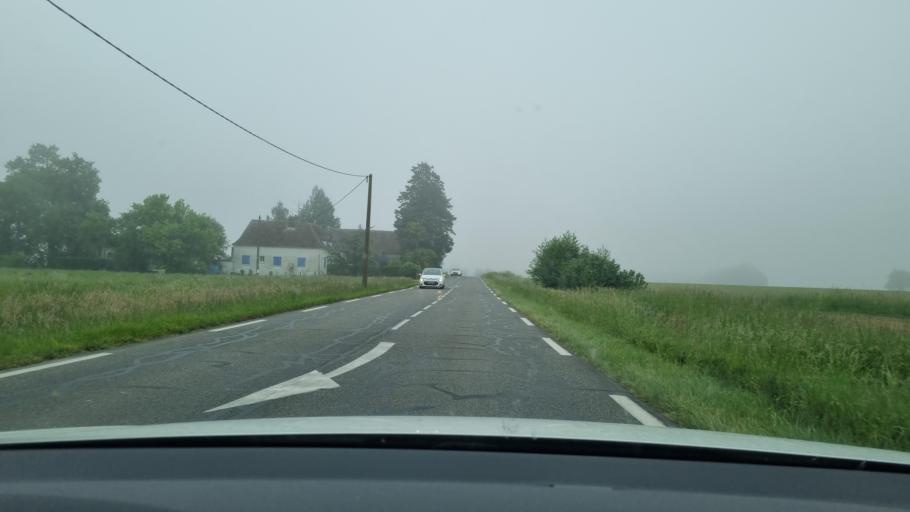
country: FR
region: Aquitaine
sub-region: Departement des Landes
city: Amou
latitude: 43.5287
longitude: -0.7009
